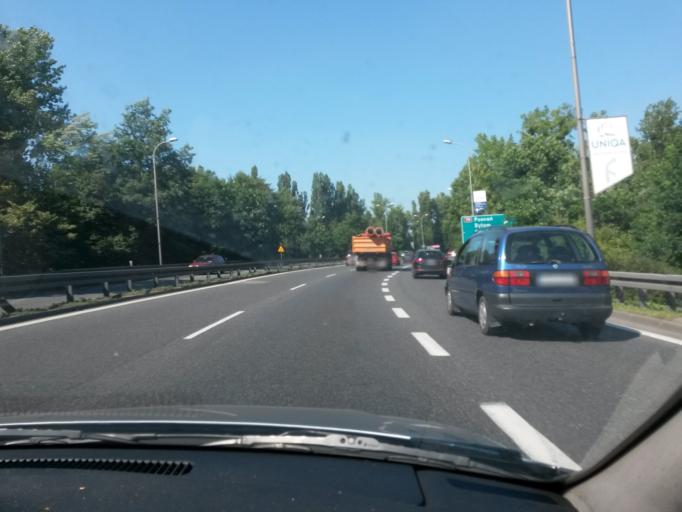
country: PL
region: Silesian Voivodeship
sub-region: Katowice
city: Katowice
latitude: 50.2630
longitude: 19.0467
